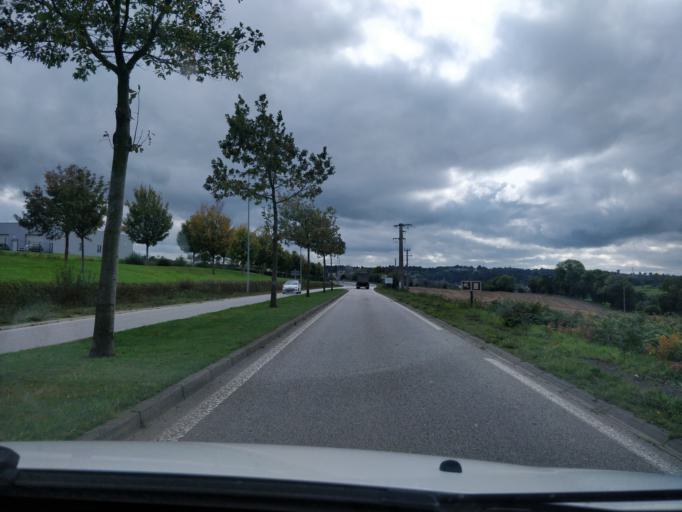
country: FR
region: Lower Normandy
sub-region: Departement de la Manche
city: Villedieu-les-Poeles
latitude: 48.8528
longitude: -1.2108
